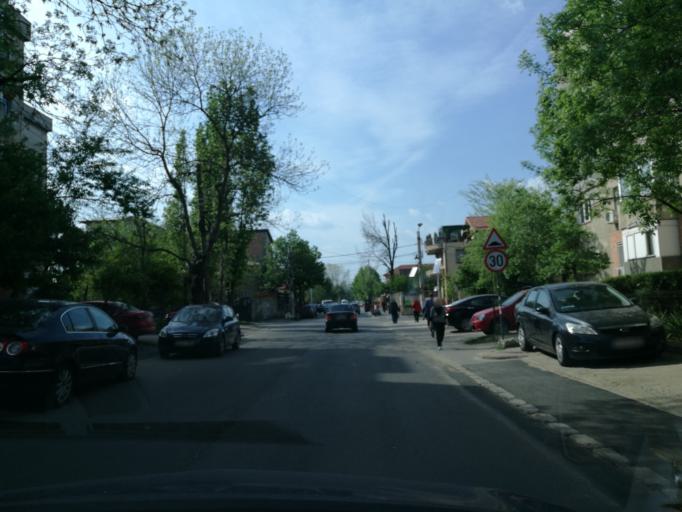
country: RO
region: Ilfov
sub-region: Comuna Chiajna
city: Rosu
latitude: 44.4416
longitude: 26.0318
